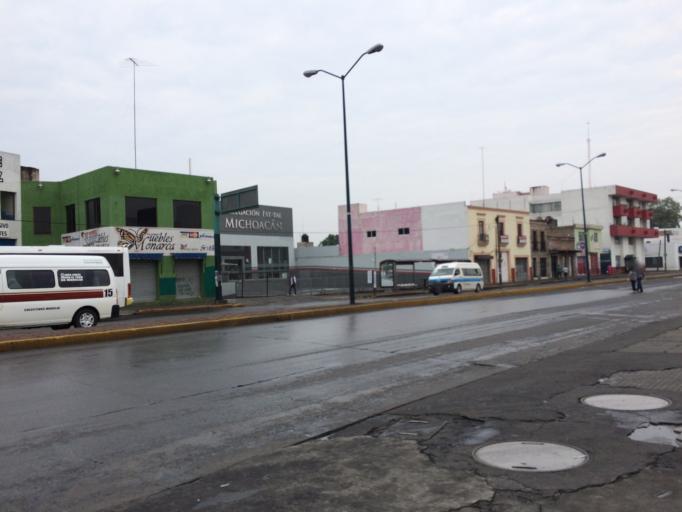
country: MX
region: Michoacan
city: Morelia
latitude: 19.7026
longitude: -101.2044
